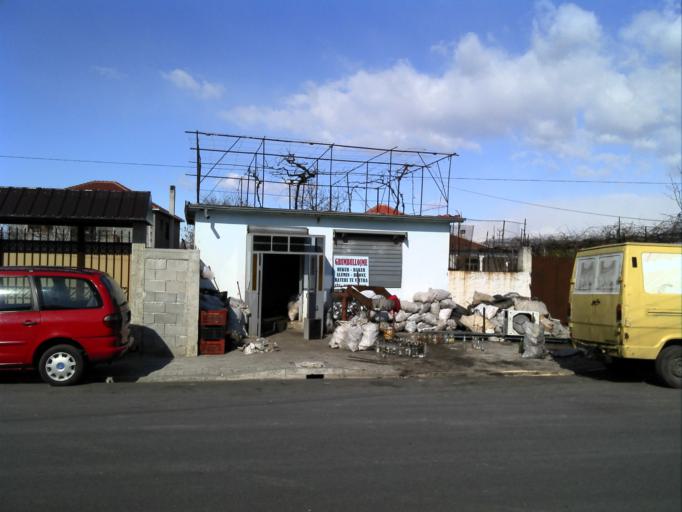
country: AL
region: Shkoder
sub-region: Rrethi i Shkodres
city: Shkoder
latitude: 42.0790
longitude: 19.5190
